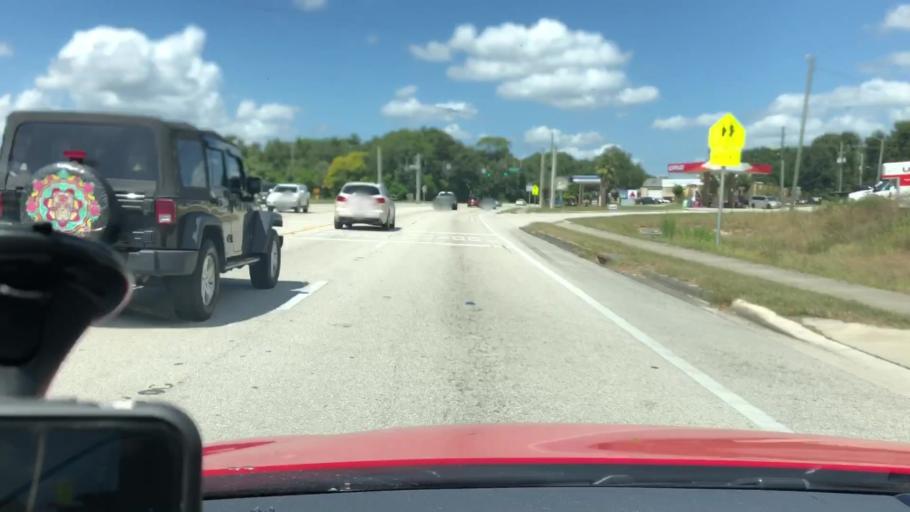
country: US
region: Florida
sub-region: Volusia County
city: West DeLand
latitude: 29.0123
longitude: -81.3225
